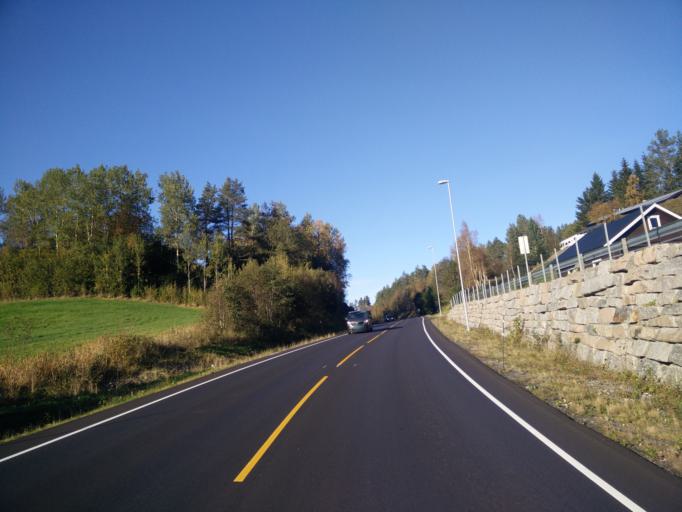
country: NO
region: More og Romsdal
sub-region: Halsa
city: Liaboen
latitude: 63.0898
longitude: 8.3522
